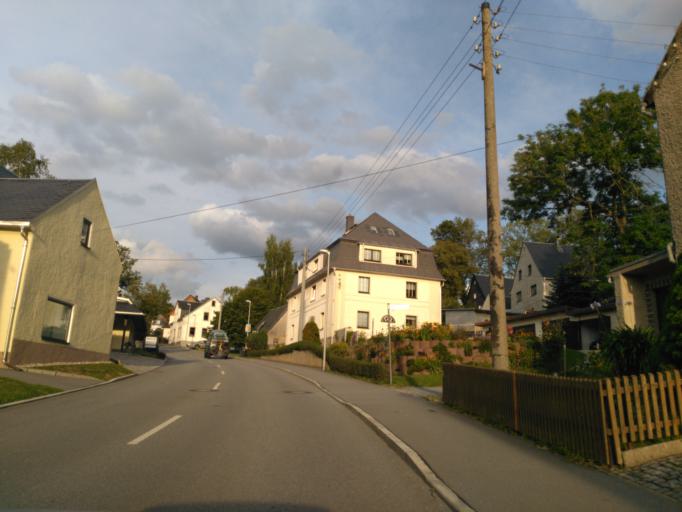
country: DE
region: Saxony
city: Annaberg-Buchholz
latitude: 50.5505
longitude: 13.0060
